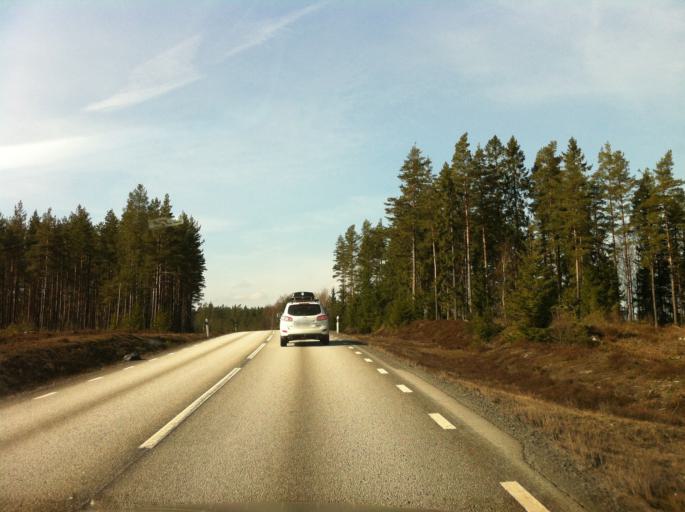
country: SE
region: Joenkoeping
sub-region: Habo Kommun
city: Habo
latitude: 57.8650
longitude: 13.9822
